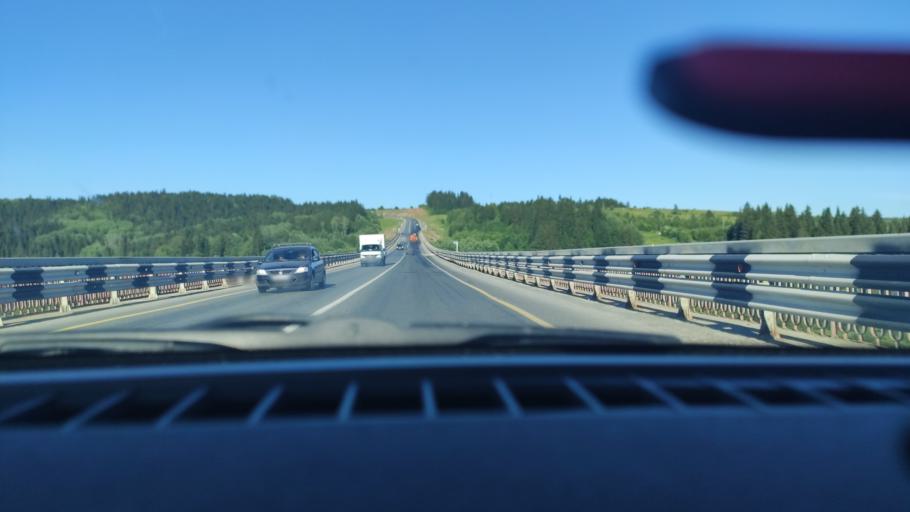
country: RU
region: Perm
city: Polazna
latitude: 58.2837
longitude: 56.4560
